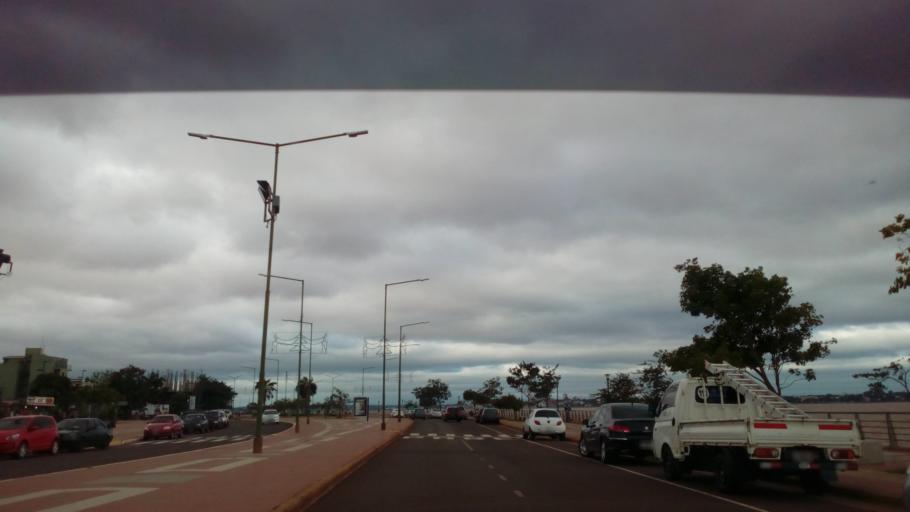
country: AR
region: Misiones
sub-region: Departamento de Capital
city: Posadas
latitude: -27.3696
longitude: -55.8847
